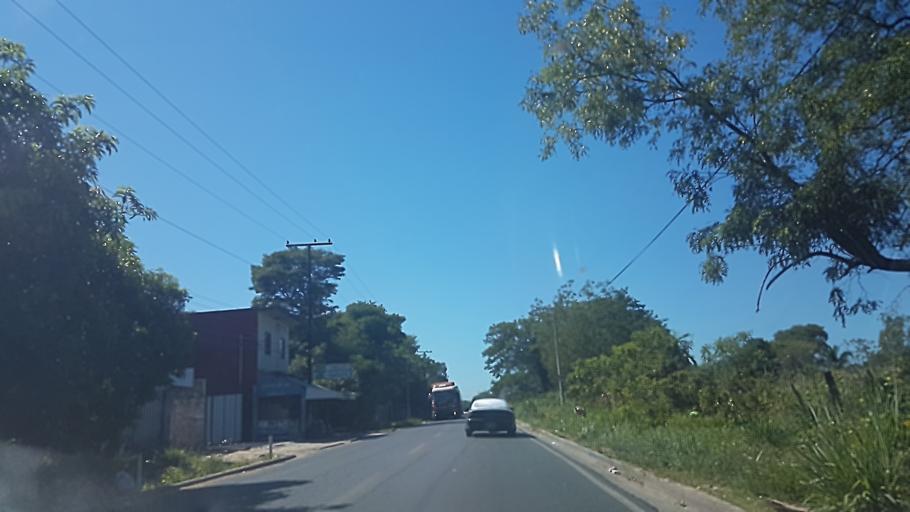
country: PY
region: Central
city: Limpio
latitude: -25.2454
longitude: -57.5051
